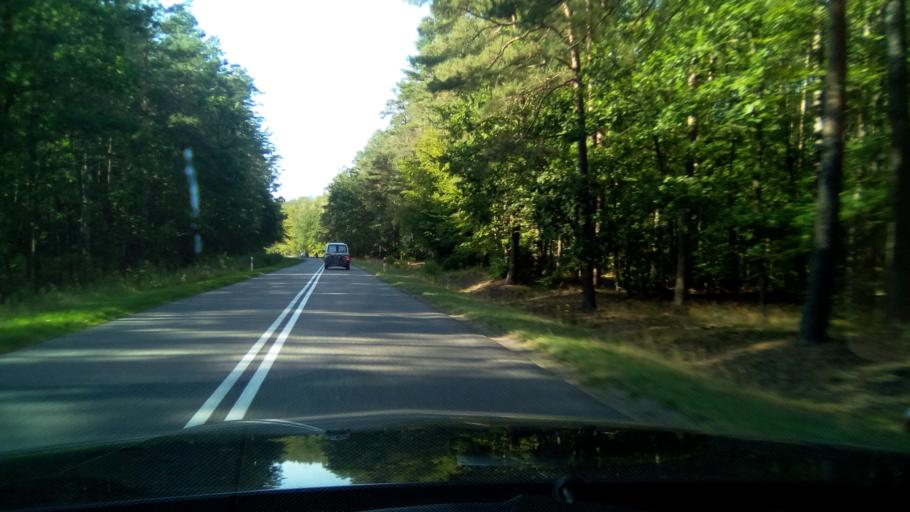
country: PL
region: West Pomeranian Voivodeship
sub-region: Powiat goleniowski
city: Przybiernow
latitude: 53.8232
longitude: 14.8082
